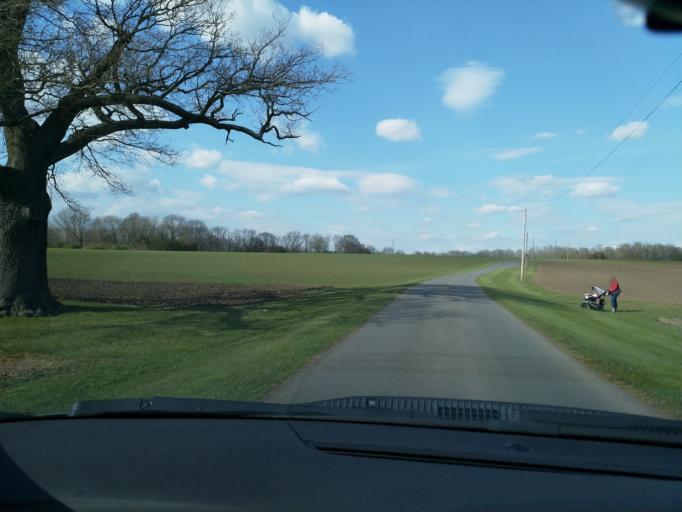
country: GB
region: England
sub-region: Warwickshire
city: Wellesbourne Mountford
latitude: 52.1732
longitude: -1.5709
